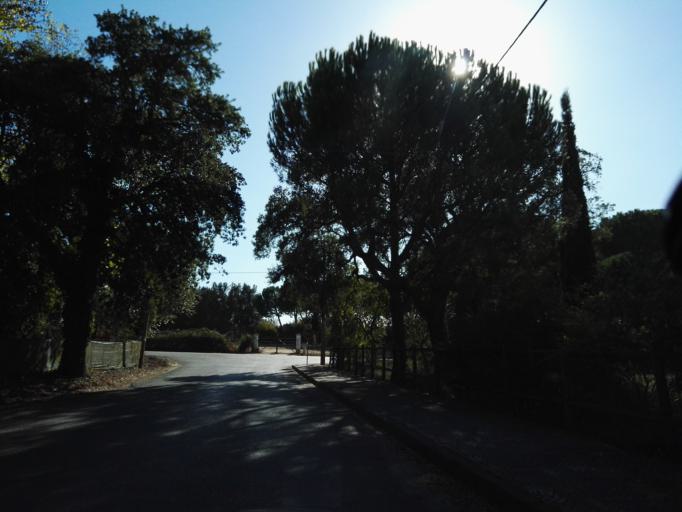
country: PT
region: Santarem
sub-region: Benavente
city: Poceirao
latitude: 38.8604
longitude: -8.7338
